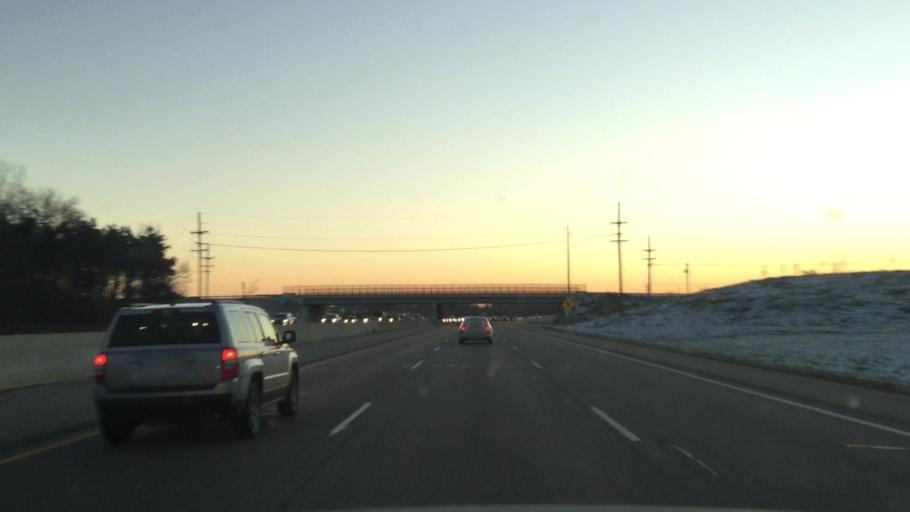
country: US
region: Michigan
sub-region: Oakland County
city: Rochester Hills
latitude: 42.6437
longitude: -83.1735
